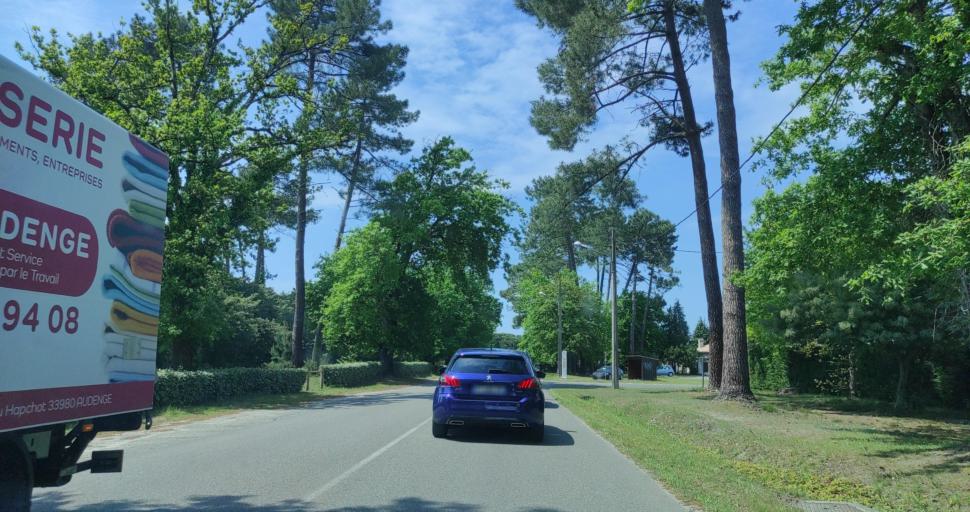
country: FR
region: Aquitaine
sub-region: Departement de la Gironde
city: Ares
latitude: 44.7605
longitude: -1.1258
